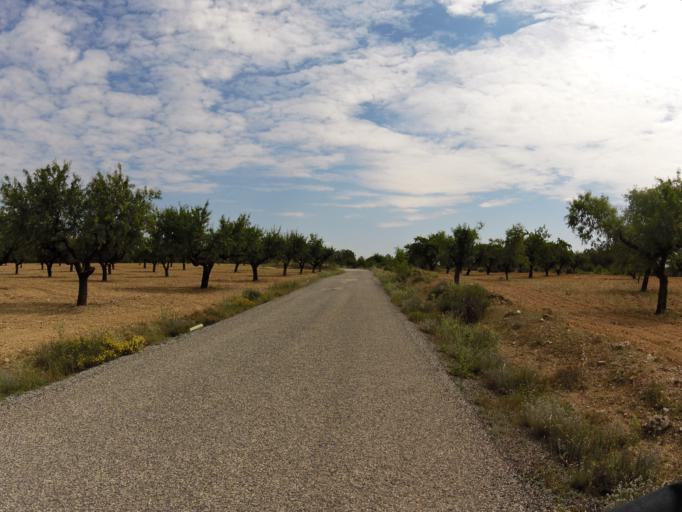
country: ES
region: Castille-La Mancha
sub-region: Provincia de Albacete
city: Casas Ibanez
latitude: 39.3554
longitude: -1.4747
